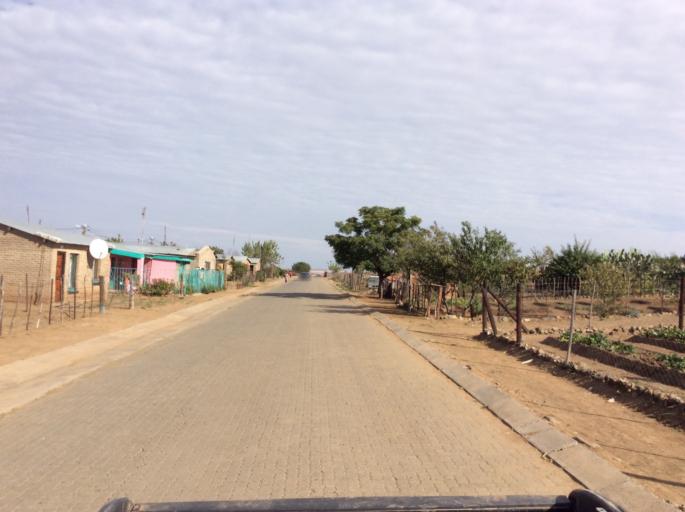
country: LS
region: Mafeteng
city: Mafeteng
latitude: -29.7175
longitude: 27.0132
